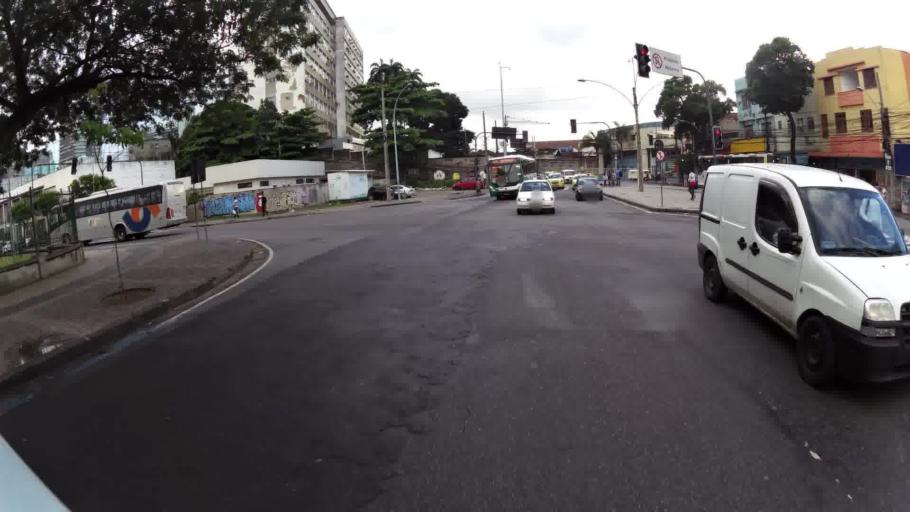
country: BR
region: Rio de Janeiro
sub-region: Rio De Janeiro
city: Rio de Janeiro
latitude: -22.9140
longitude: -43.2048
